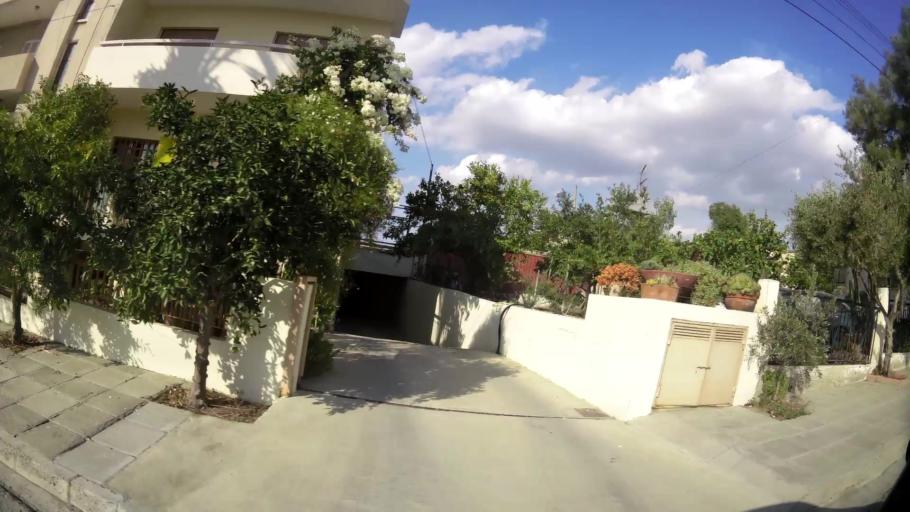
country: CY
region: Lefkosia
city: Nicosia
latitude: 35.1789
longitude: 33.3377
